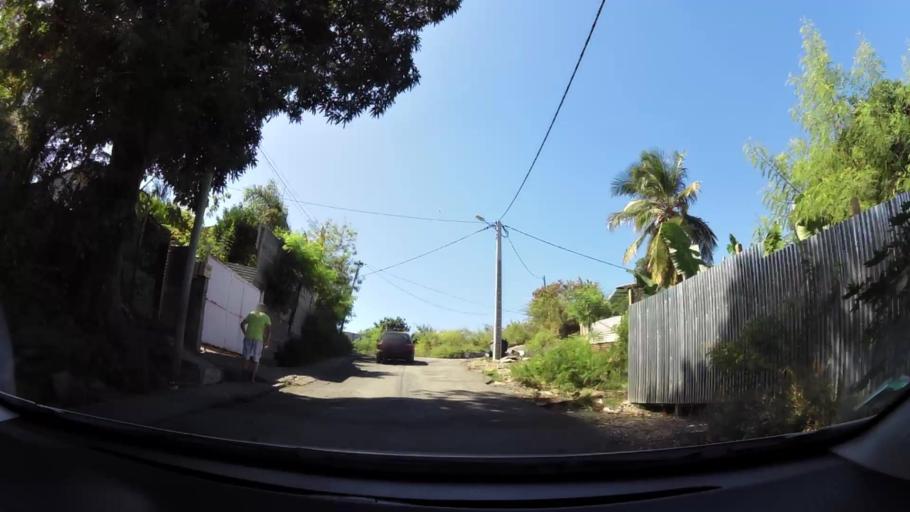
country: YT
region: Pamandzi
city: Pamandzi
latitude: -12.7981
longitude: 45.2809
